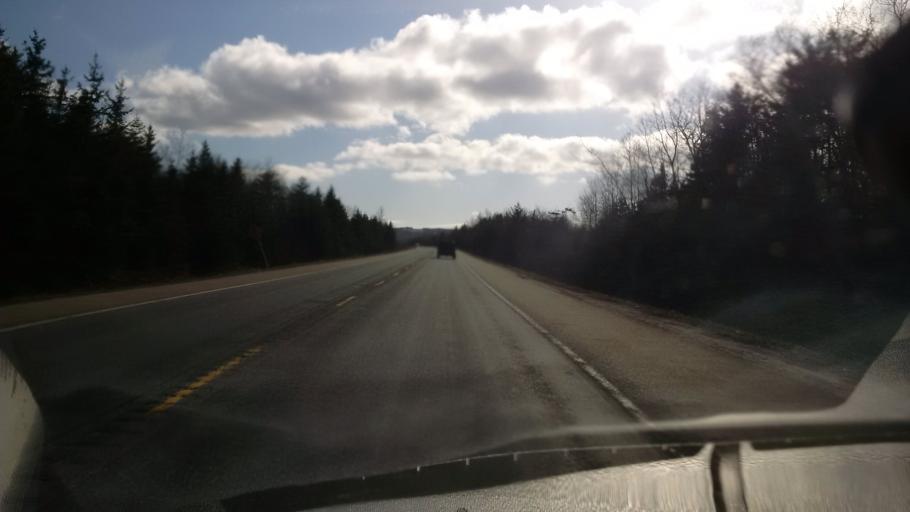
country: CA
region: Nova Scotia
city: Antigonish
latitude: 45.5770
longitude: -62.1068
